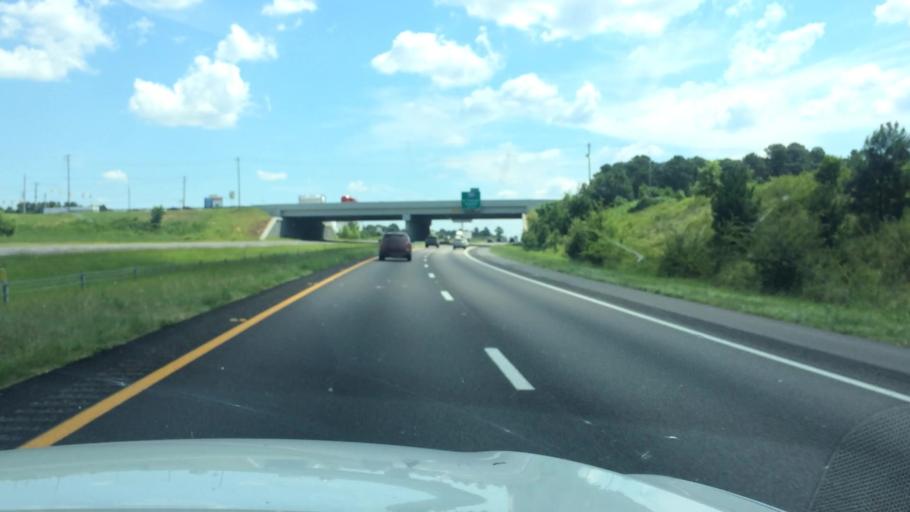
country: US
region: South Carolina
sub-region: Aiken County
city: Belvedere
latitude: 33.5637
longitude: -81.9387
